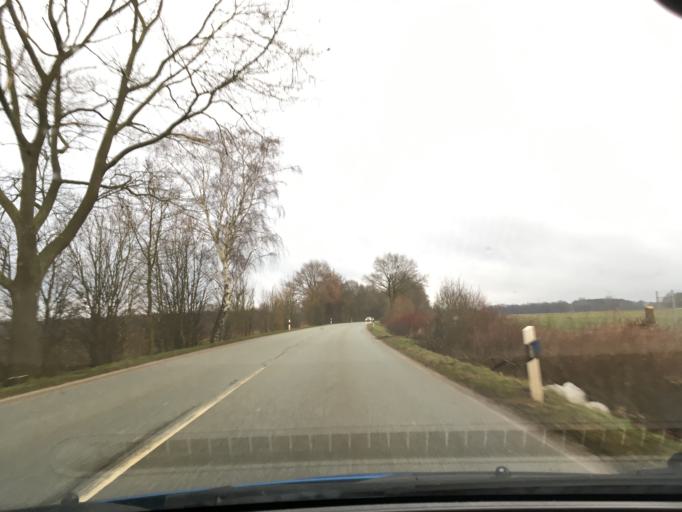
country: DE
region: Schleswig-Holstein
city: Siebeneichen
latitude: 53.5140
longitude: 10.6133
